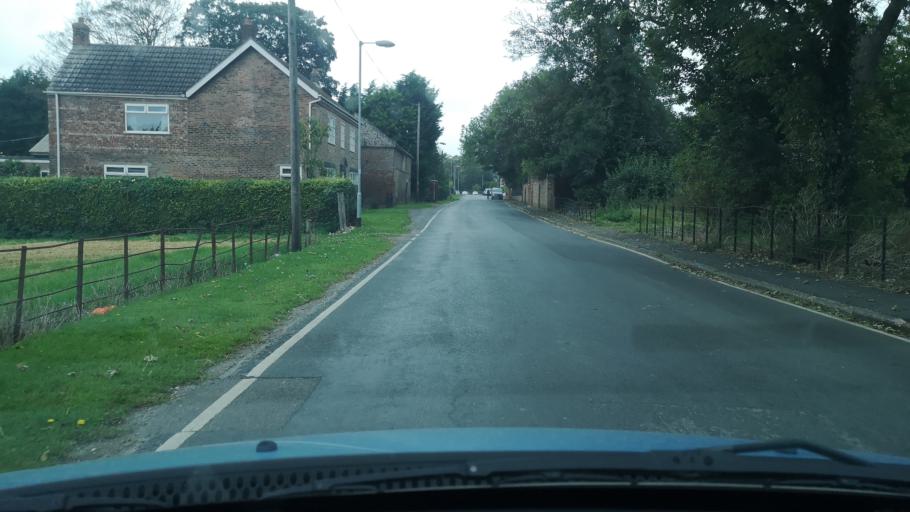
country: GB
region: England
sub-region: East Riding of Yorkshire
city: Laxton
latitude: 53.6987
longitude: -0.7962
